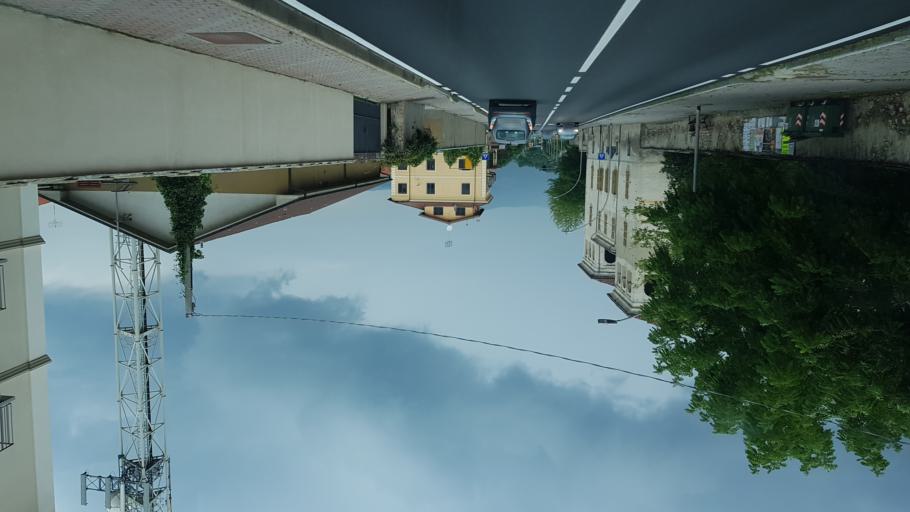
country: IT
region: Piedmont
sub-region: Provincia di Cuneo
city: Caraglio
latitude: 44.4211
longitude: 7.4322
